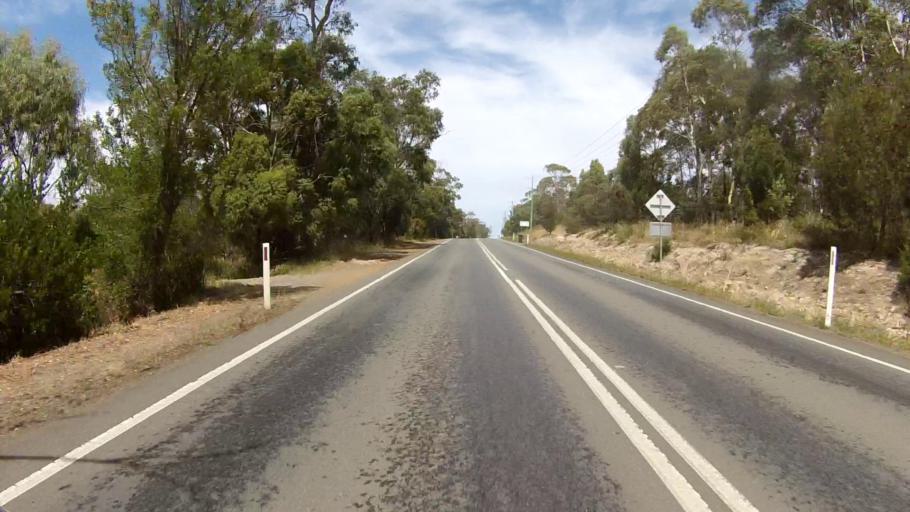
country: AU
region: Tasmania
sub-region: Clarence
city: Sandford
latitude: -42.9668
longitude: 147.5029
